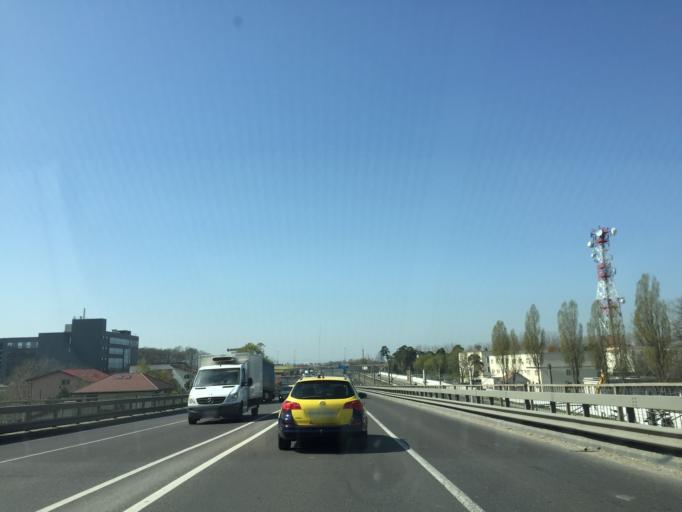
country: RO
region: Ilfov
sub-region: Comuna Otopeni
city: Otopeni
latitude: 44.5363
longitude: 26.0749
